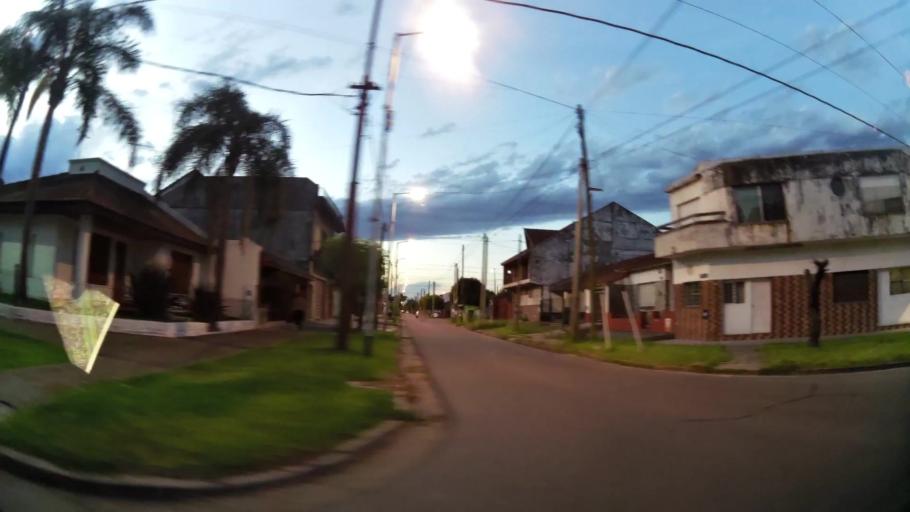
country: AR
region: Buenos Aires
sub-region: Partido de Avellaneda
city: Avellaneda
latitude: -34.6924
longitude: -58.3127
